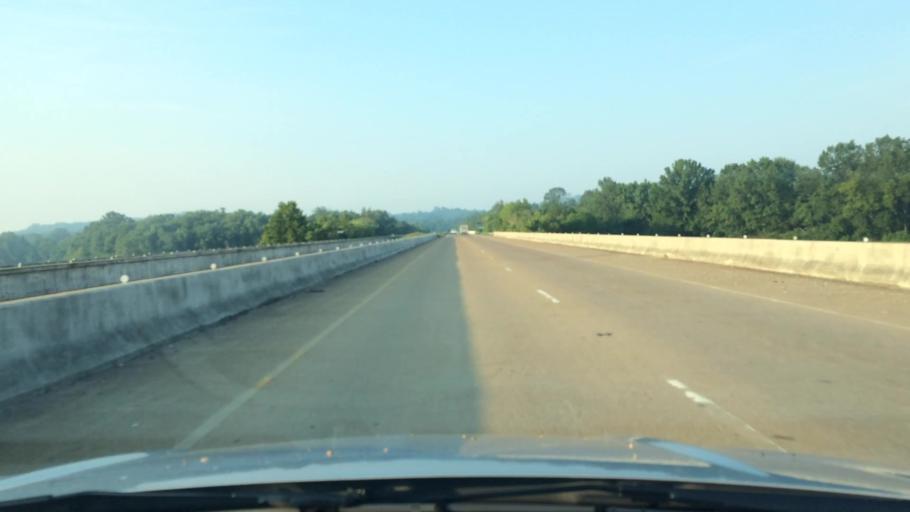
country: US
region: Tennessee
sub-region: Giles County
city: Pulaski
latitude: 35.1996
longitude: -87.0636
